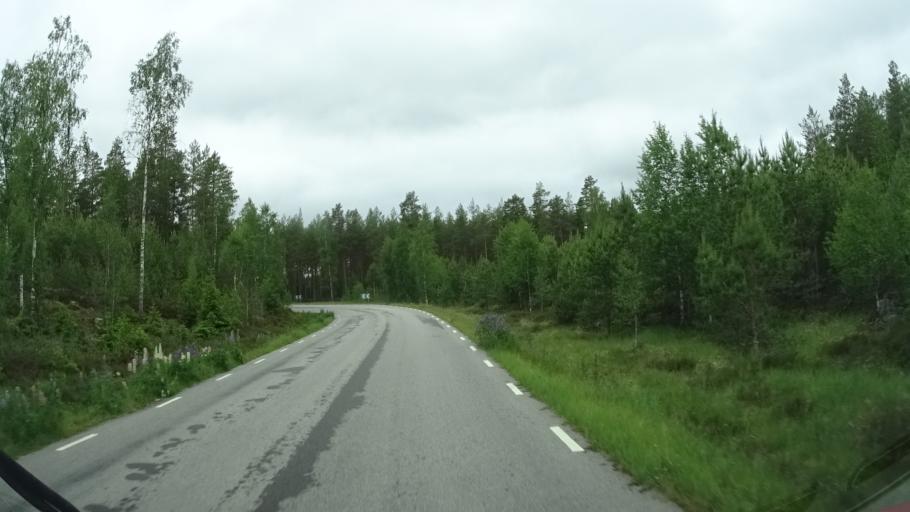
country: SE
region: Joenkoeping
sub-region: Eksjo Kommun
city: Mariannelund
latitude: 57.7002
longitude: 15.6246
